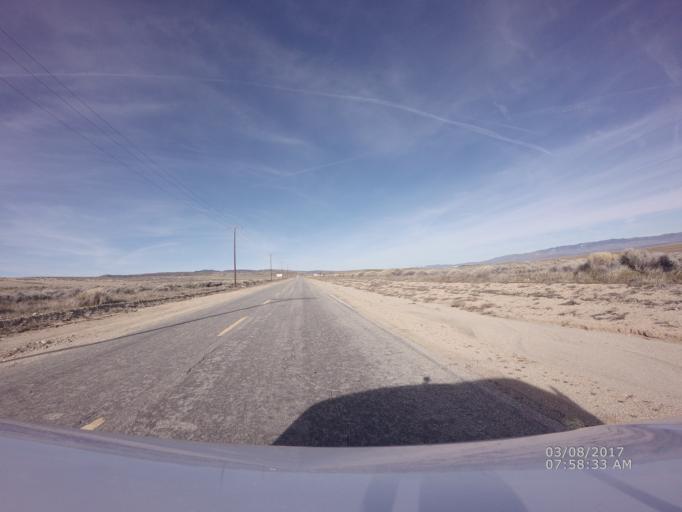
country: US
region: California
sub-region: Los Angeles County
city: Green Valley
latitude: 34.7246
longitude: -118.4055
